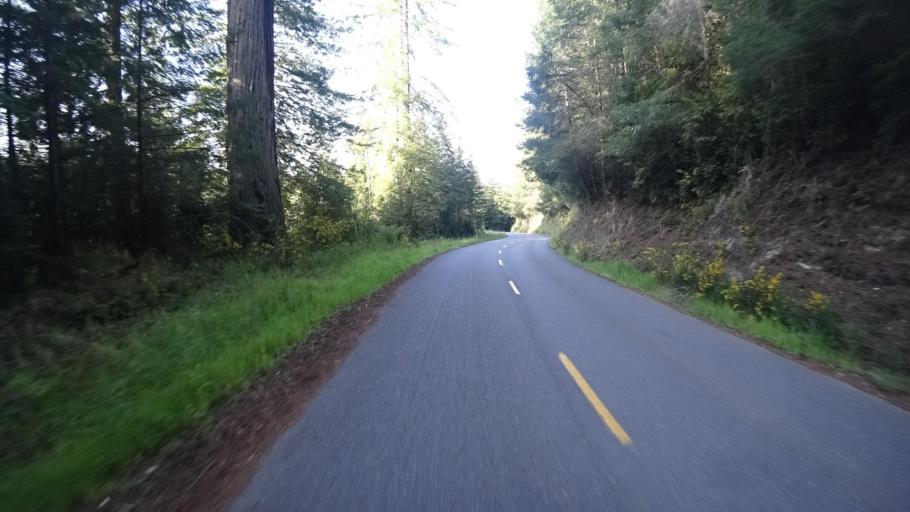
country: US
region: California
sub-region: Humboldt County
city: Bayside
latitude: 40.7558
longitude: -124.0399
